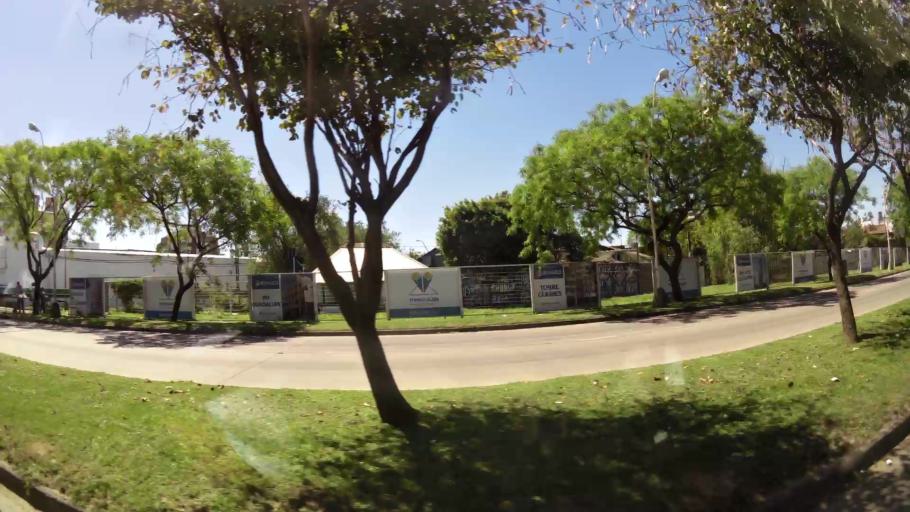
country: AR
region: Santa Fe
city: Santa Fe de la Vera Cruz
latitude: -31.6457
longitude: -60.6964
